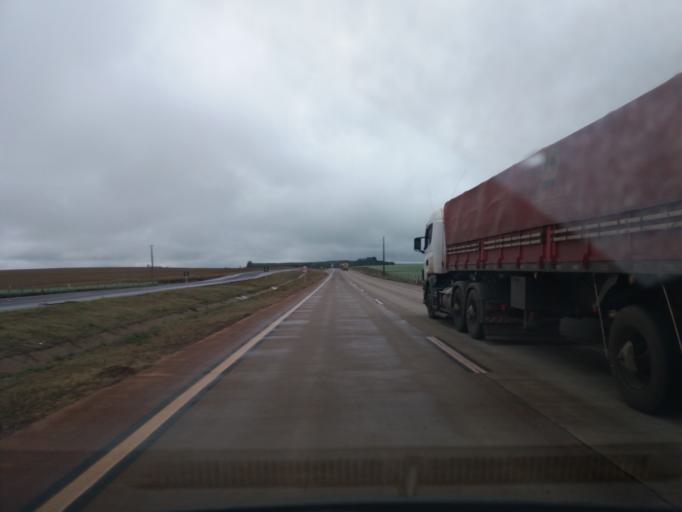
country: BR
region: Parana
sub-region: Cascavel
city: Cascavel
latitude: -25.0732
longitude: -53.5738
